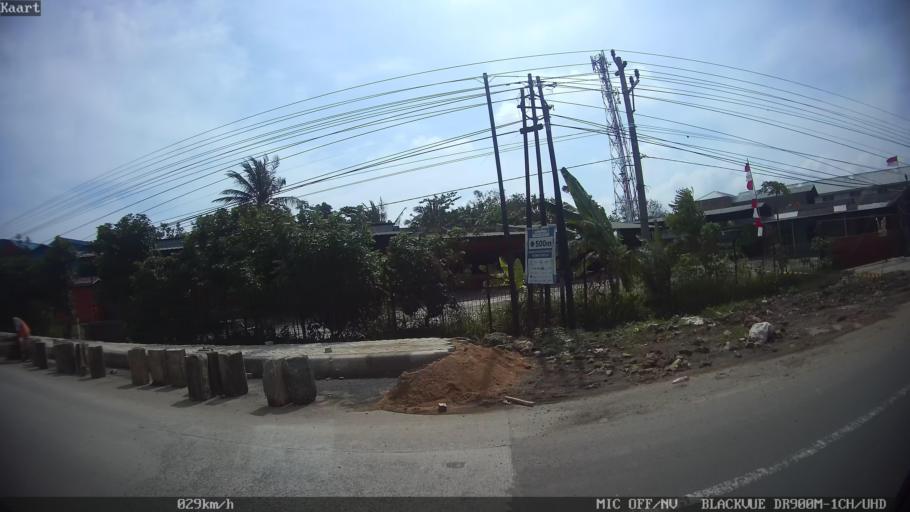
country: ID
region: Lampung
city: Kedaton
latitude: -5.3906
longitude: 105.2884
